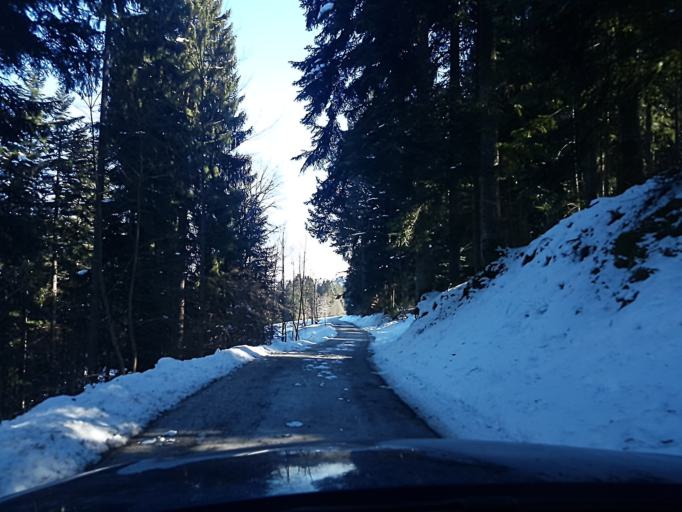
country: DE
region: Baden-Wuerttemberg
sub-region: Freiburg Region
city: Schramberg
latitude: 48.2281
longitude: 8.3718
